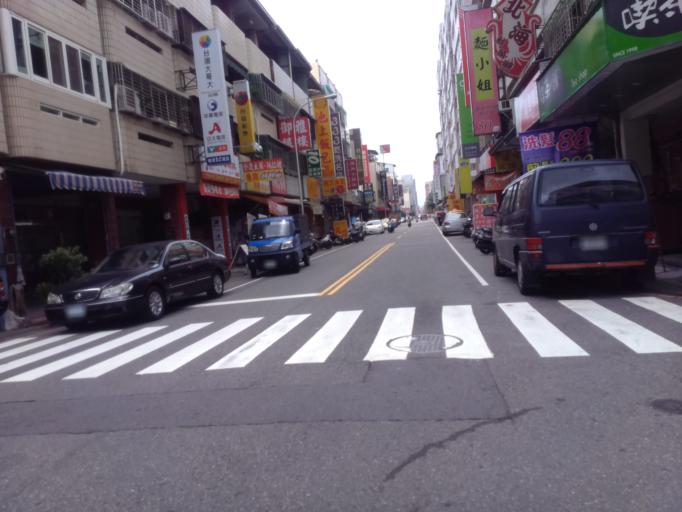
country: TW
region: Taiwan
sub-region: Taichung City
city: Taichung
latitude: 24.1714
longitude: 120.6769
